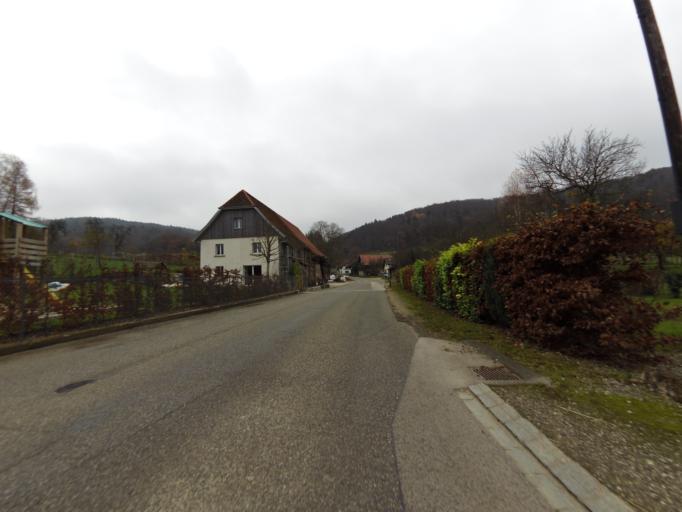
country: CH
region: Jura
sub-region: Porrentruy District
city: Alle
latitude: 47.4235
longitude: 7.2113
